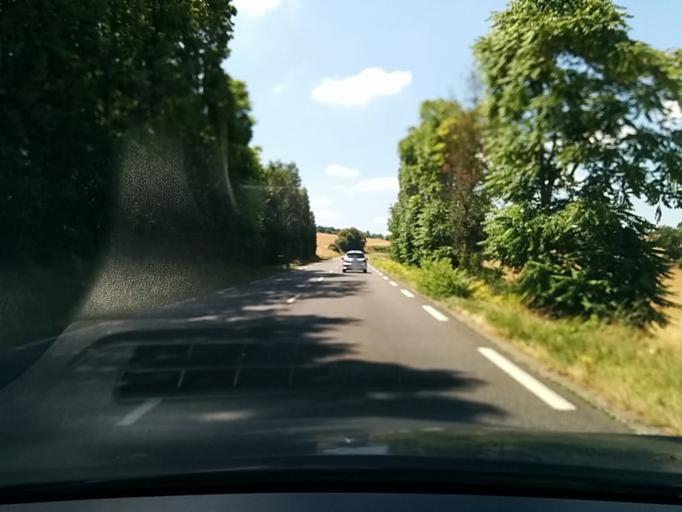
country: FR
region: Midi-Pyrenees
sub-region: Departement du Gers
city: Vic-Fezensac
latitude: 43.7467
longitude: 0.3446
